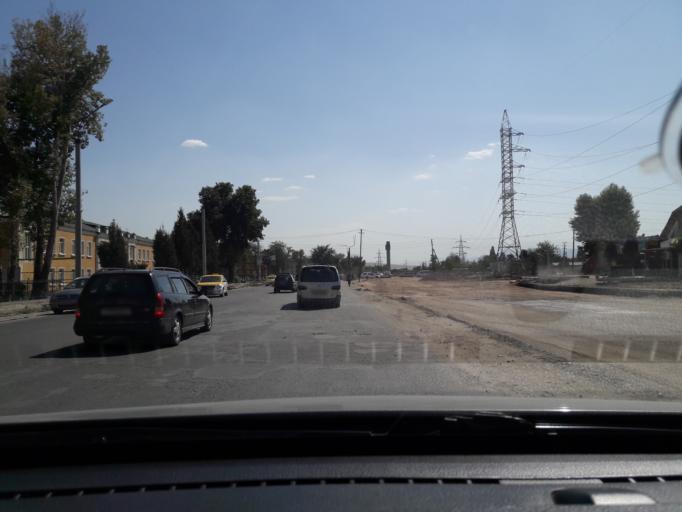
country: TJ
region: Dushanbe
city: Dushanbe
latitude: 38.5334
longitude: 68.7378
